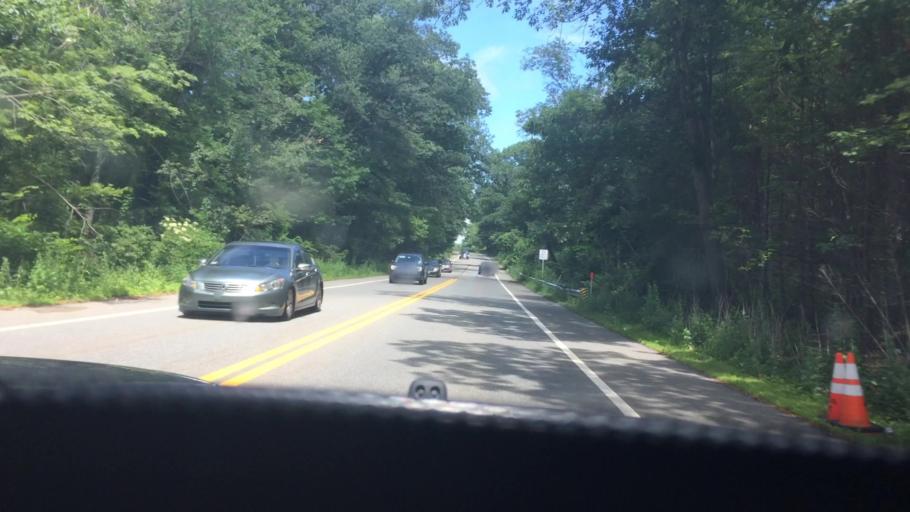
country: US
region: Massachusetts
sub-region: Essex County
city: Andover
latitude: 42.6303
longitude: -71.1150
